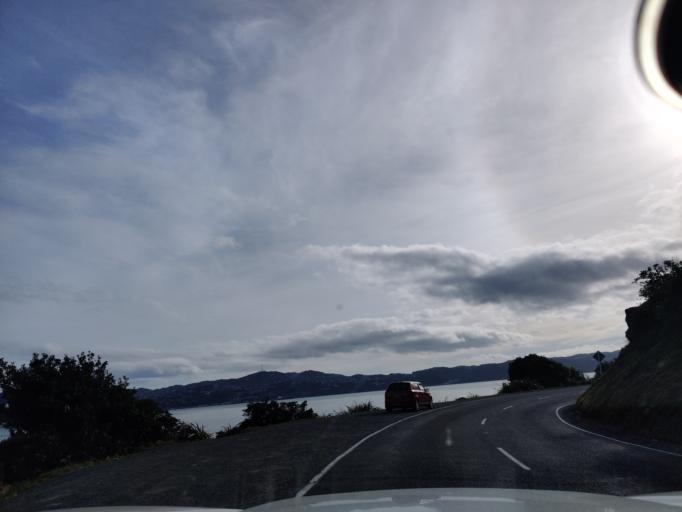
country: NZ
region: Wellington
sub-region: Wellington City
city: Wellington
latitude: -41.2999
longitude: 174.8173
